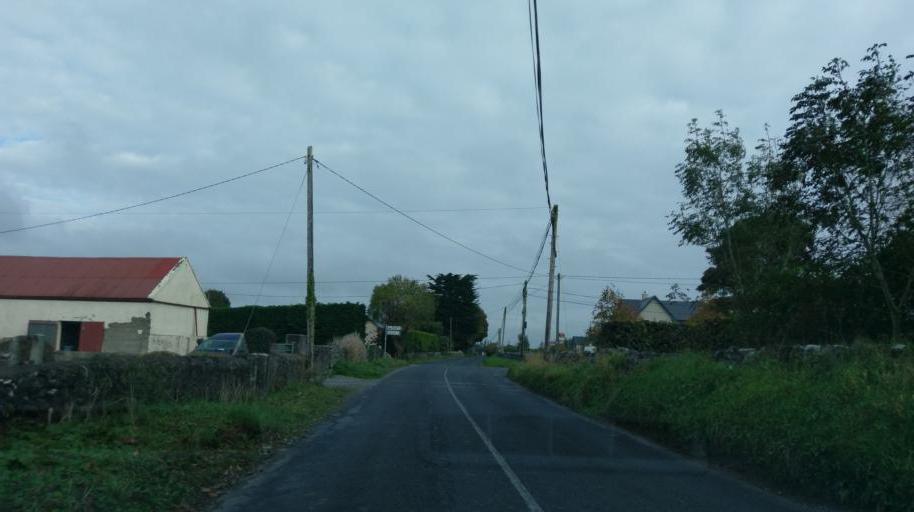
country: IE
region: Connaught
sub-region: County Galway
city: Athenry
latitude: 53.3486
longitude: -8.7084
